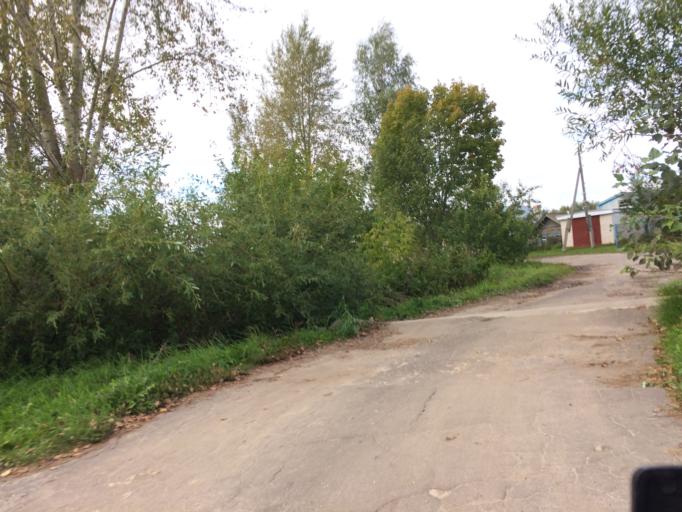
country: RU
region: Mariy-El
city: Yoshkar-Ola
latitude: 56.6527
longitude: 48.0146
